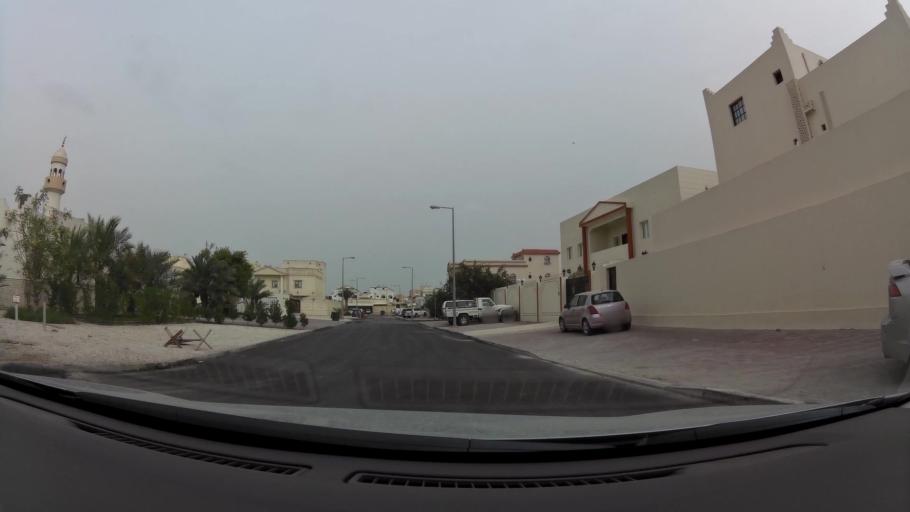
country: QA
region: Baladiyat ad Dawhah
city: Doha
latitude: 25.2421
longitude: 51.5217
